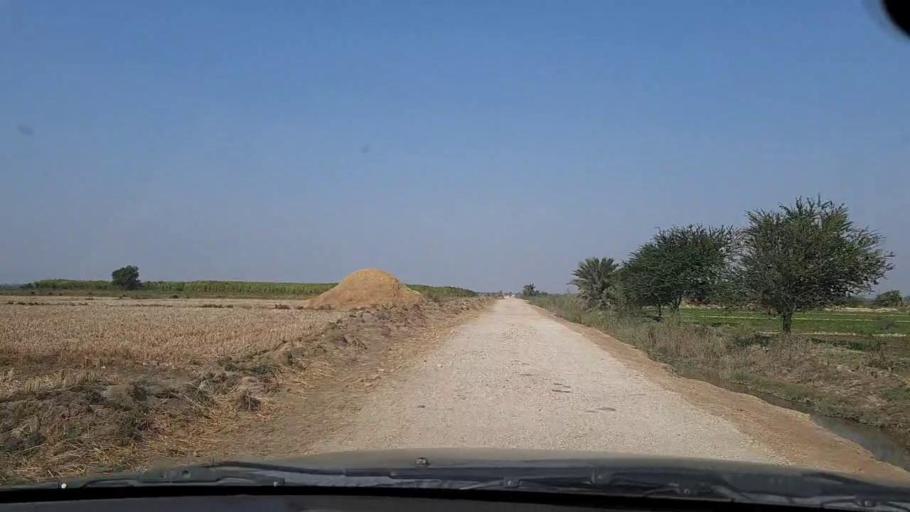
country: PK
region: Sindh
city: Mirpur Sakro
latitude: 24.3642
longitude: 67.6830
